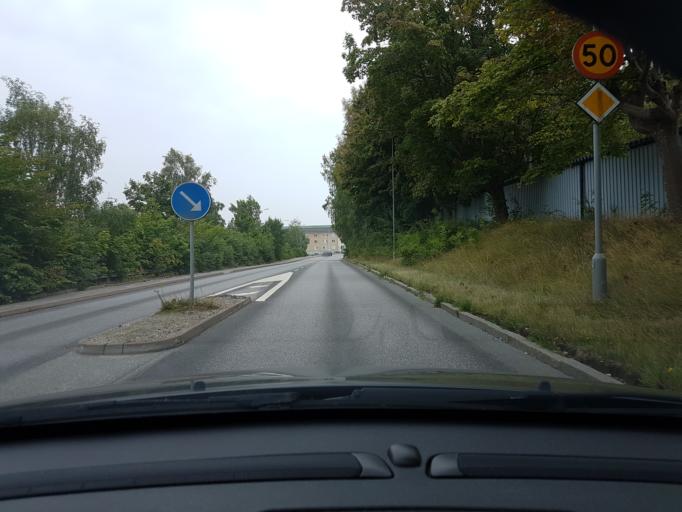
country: SE
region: Vaestra Goetaland
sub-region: Goteborg
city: Majorna
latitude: 57.6461
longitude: 11.8940
